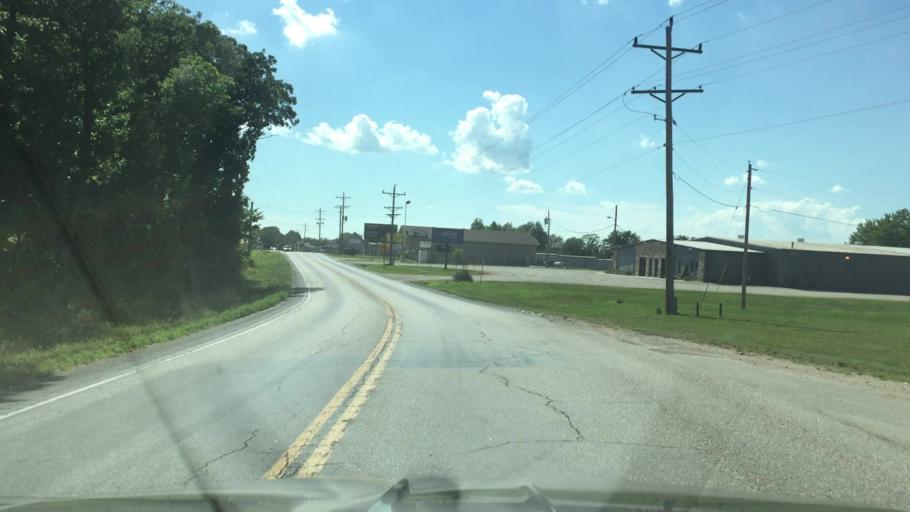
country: US
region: Missouri
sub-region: Camden County
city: Osage Beach
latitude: 38.1396
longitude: -92.5819
